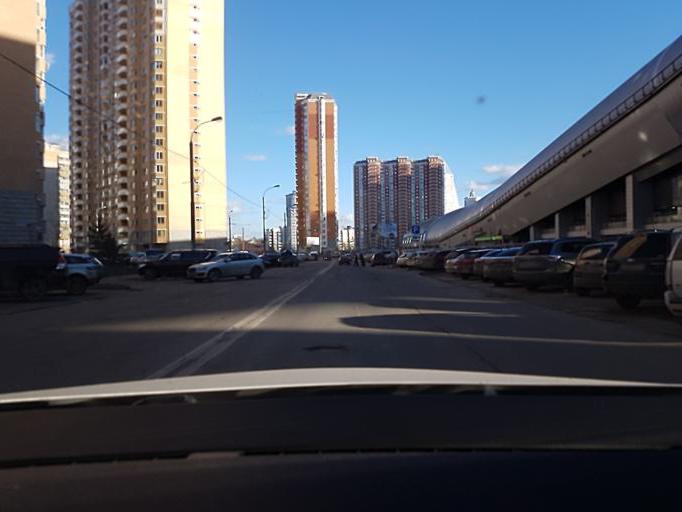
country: RU
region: Moskovskaya
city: Pavshino
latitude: 55.8167
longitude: 37.3632
